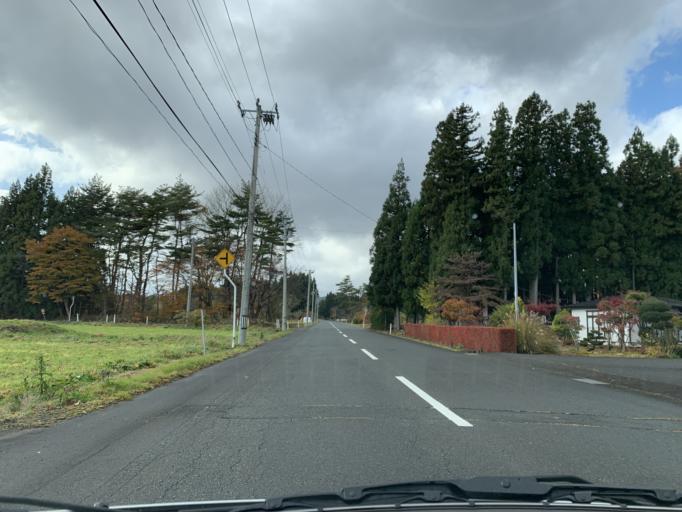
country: JP
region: Iwate
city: Mizusawa
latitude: 39.1111
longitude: 140.9830
